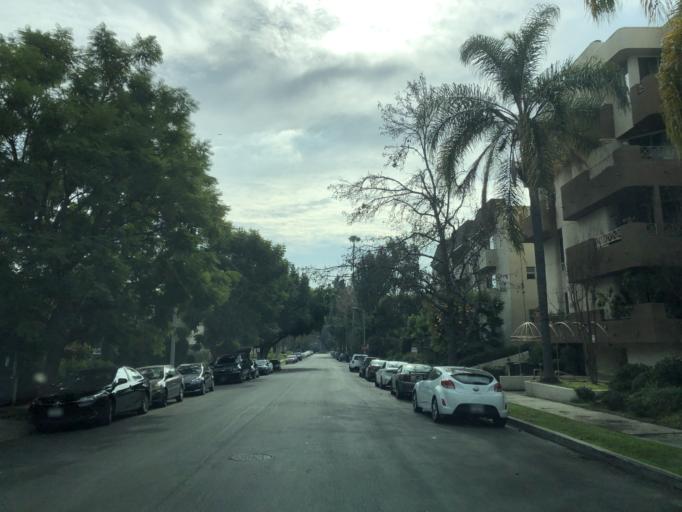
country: US
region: California
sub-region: Los Angeles County
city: Hollywood
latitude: 34.0680
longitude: -118.3163
